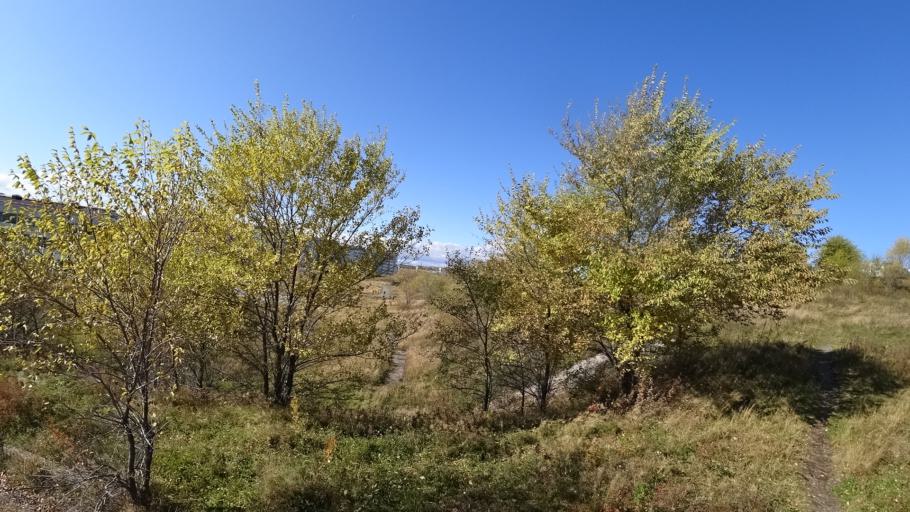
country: RU
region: Khabarovsk Krai
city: Amursk
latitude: 50.2391
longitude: 136.9178
